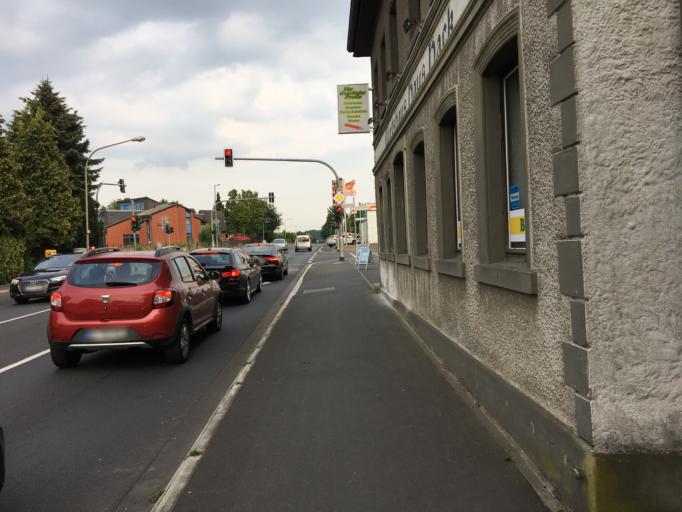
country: DE
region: North Rhine-Westphalia
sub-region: Regierungsbezirk Koln
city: Rosrath
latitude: 50.8975
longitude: 7.1692
